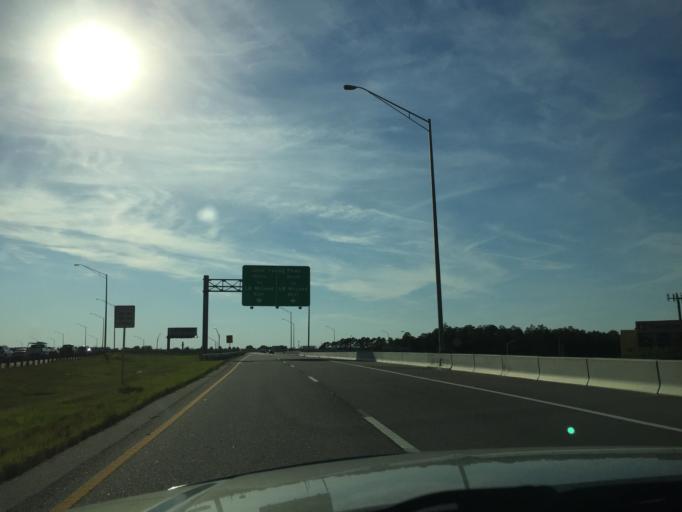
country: US
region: Florida
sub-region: Orange County
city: Holden Heights
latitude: 28.5096
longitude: -81.4171
